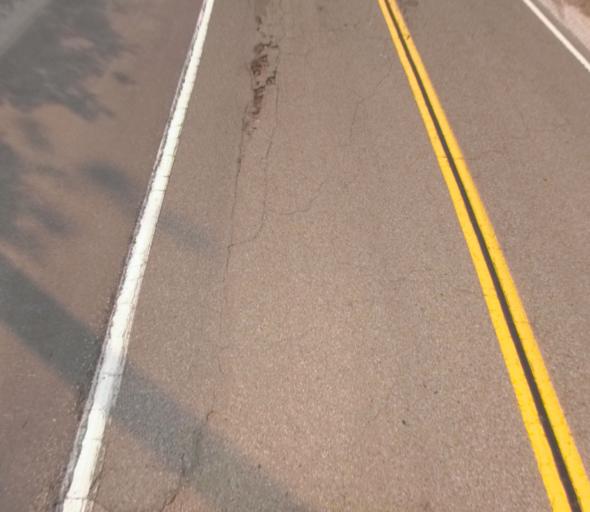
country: US
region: California
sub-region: Madera County
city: Oakhurst
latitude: 37.3039
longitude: -119.5815
